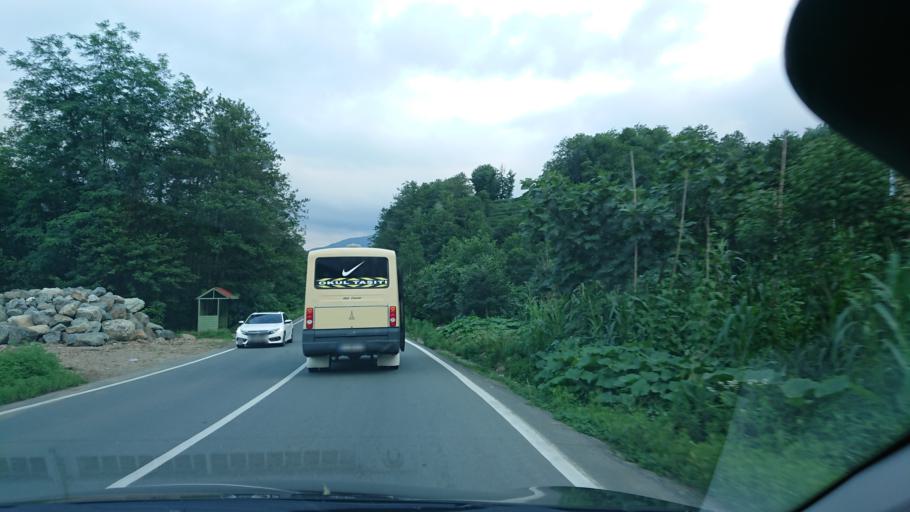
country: TR
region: Rize
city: Cayeli
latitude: 41.0699
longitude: 40.7120
